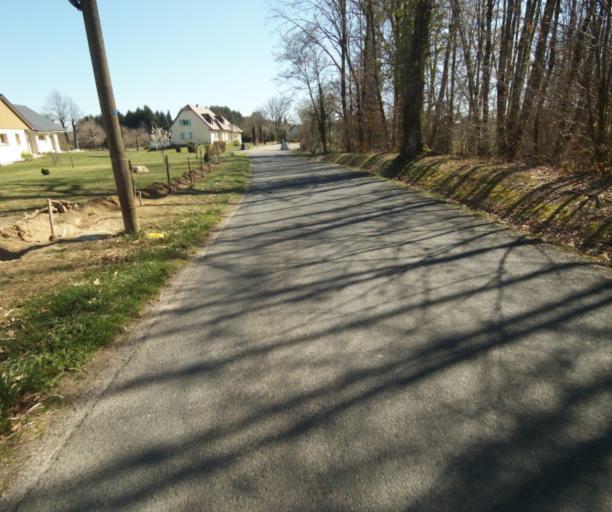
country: FR
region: Limousin
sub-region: Departement de la Correze
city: Saint-Mexant
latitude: 45.2884
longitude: 1.6566
